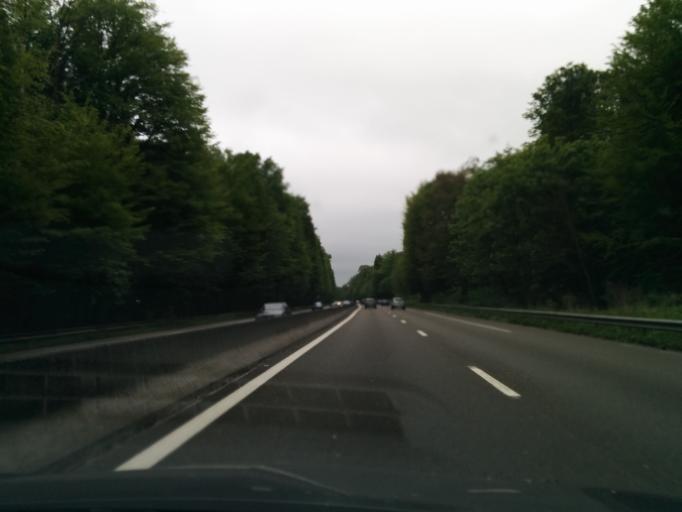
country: FR
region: Ile-de-France
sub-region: Departement des Yvelines
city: Saint-Nom-la-Breteche
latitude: 48.8815
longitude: 2.0159
